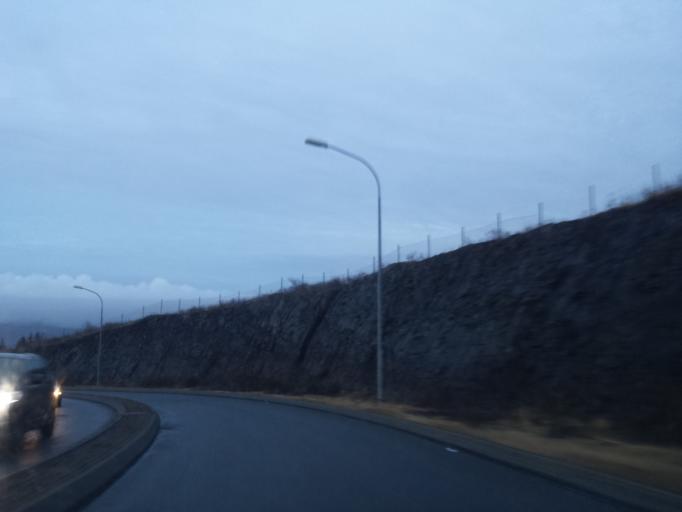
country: IS
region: Capital Region
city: Mosfellsbaer
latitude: 64.1409
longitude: -21.7496
